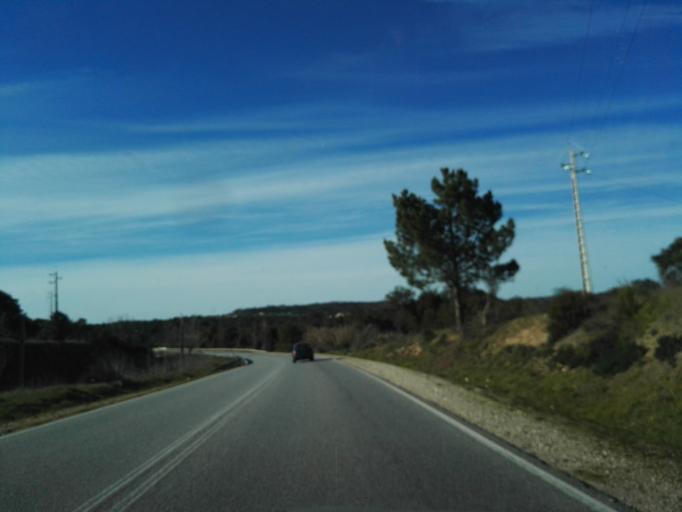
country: PT
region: Santarem
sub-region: Abrantes
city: Alferrarede
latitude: 39.4683
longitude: -8.0602
